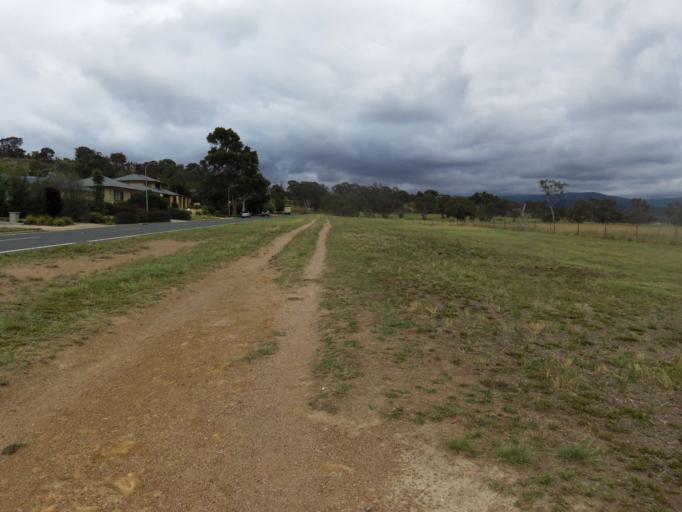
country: AU
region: Australian Capital Territory
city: Macquarie
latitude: -35.3480
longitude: 149.0260
